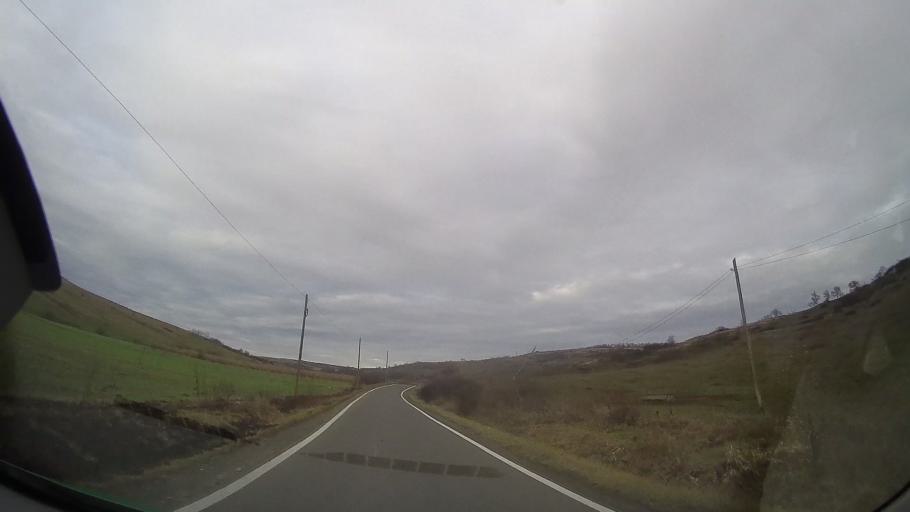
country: RO
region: Mures
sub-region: Comuna Cozma
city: Cozma
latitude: 46.7981
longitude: 24.5386
